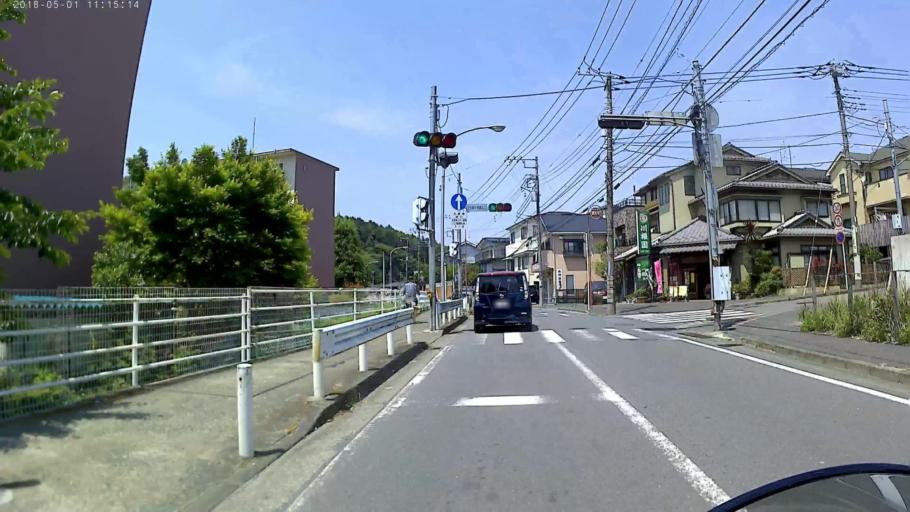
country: JP
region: Kanagawa
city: Minami-rinkan
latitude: 35.4897
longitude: 139.5402
